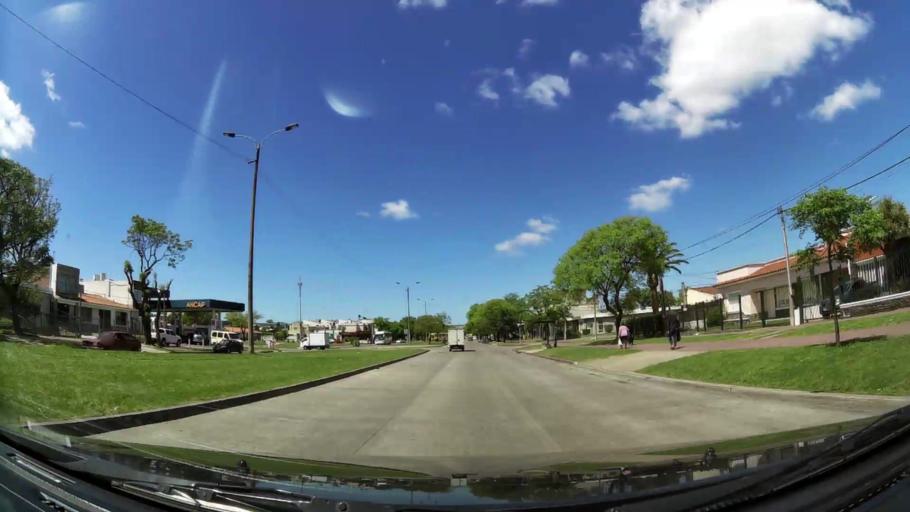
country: UY
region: Montevideo
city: Montevideo
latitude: -34.8581
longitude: -56.1506
